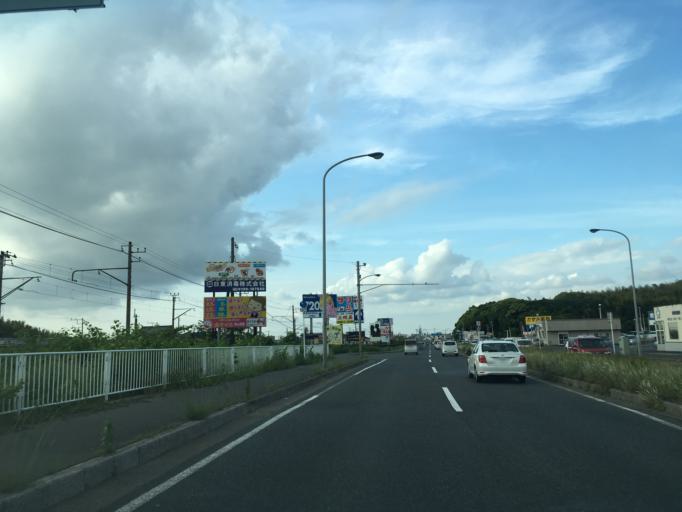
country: JP
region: Chiba
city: Kisarazu
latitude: 35.3593
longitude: 139.9211
